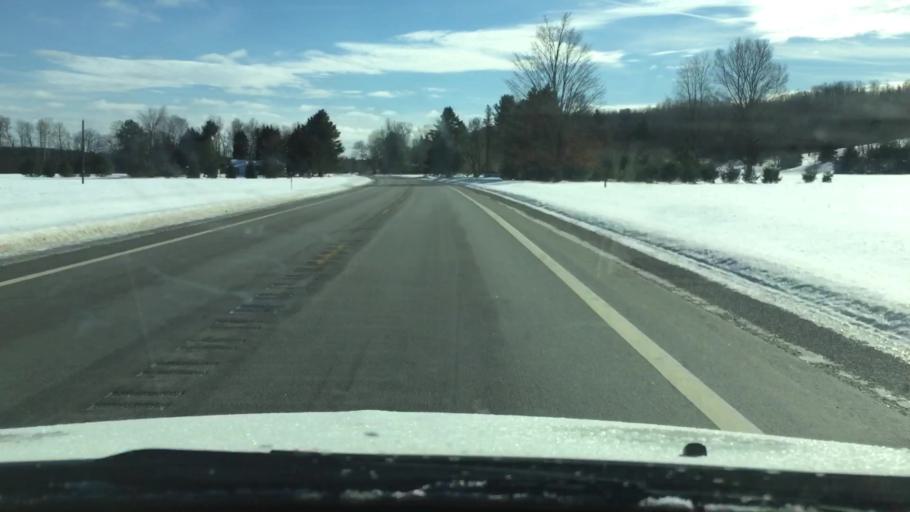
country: US
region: Michigan
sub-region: Charlevoix County
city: East Jordan
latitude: 45.0690
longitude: -85.0848
